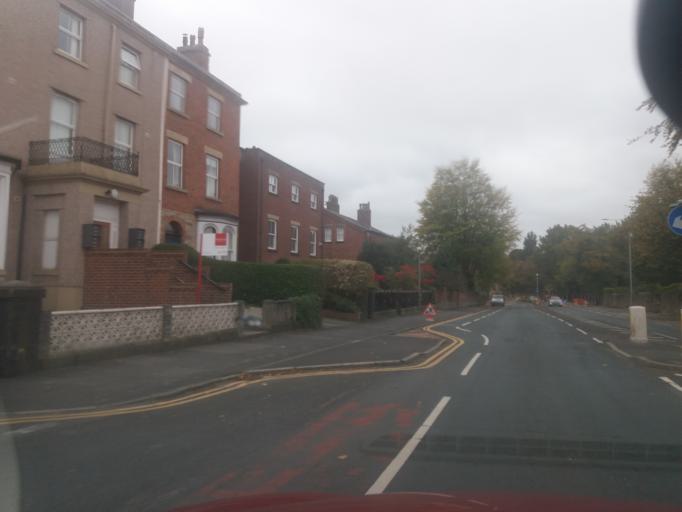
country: GB
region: England
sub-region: Lancashire
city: Chorley
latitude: 53.6571
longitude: -2.6324
